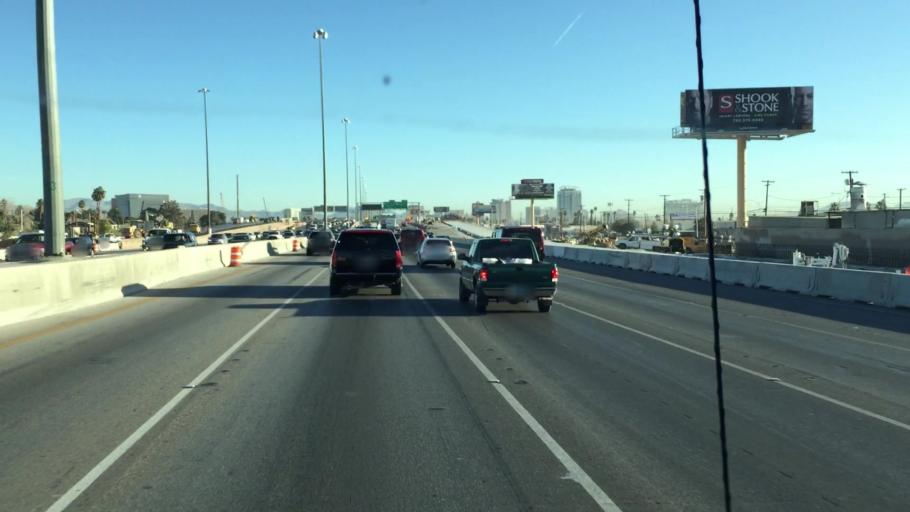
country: US
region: Nevada
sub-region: Clark County
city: Las Vegas
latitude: 36.1482
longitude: -115.1671
